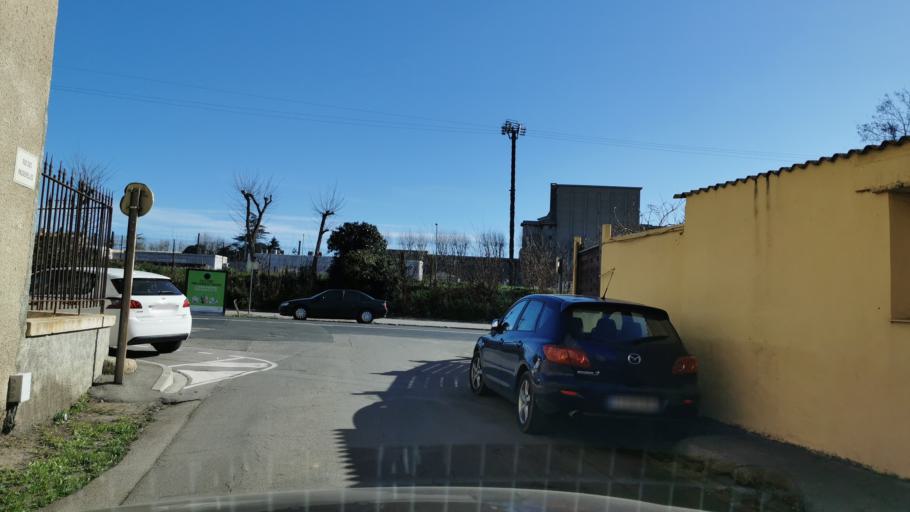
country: FR
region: Languedoc-Roussillon
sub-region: Departement de l'Aude
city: Narbonne
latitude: 43.1882
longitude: 3.0001
